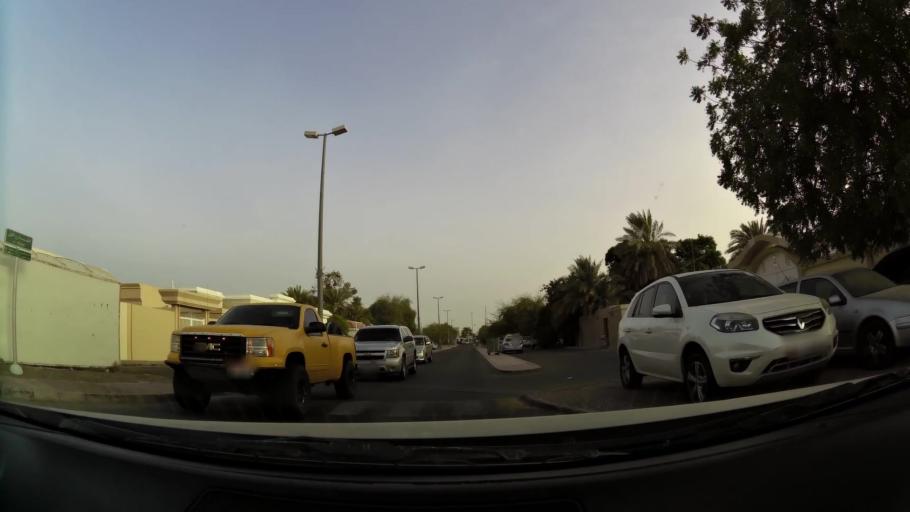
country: AE
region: Abu Dhabi
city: Al Ain
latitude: 24.2440
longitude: 55.7331
